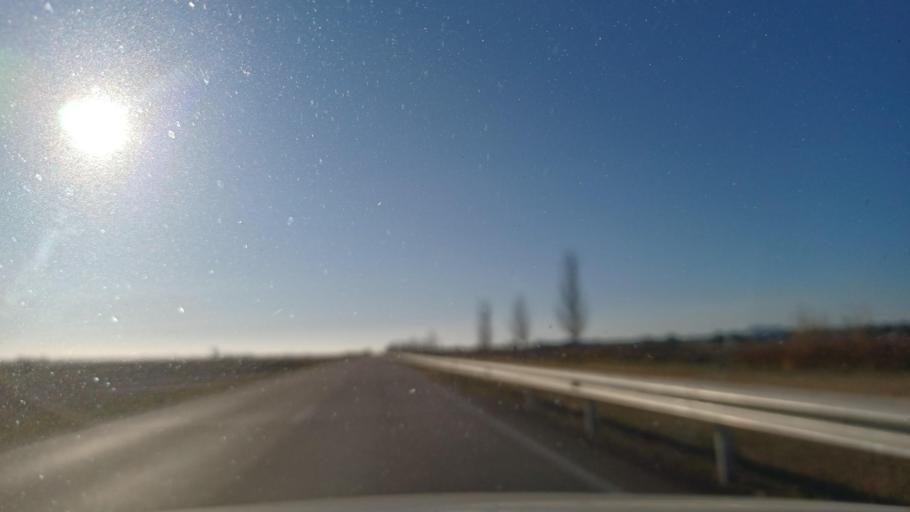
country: ES
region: Catalonia
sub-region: Provincia de Tarragona
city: Sant Carles de la Rapita
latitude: 40.6571
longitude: 0.5936
